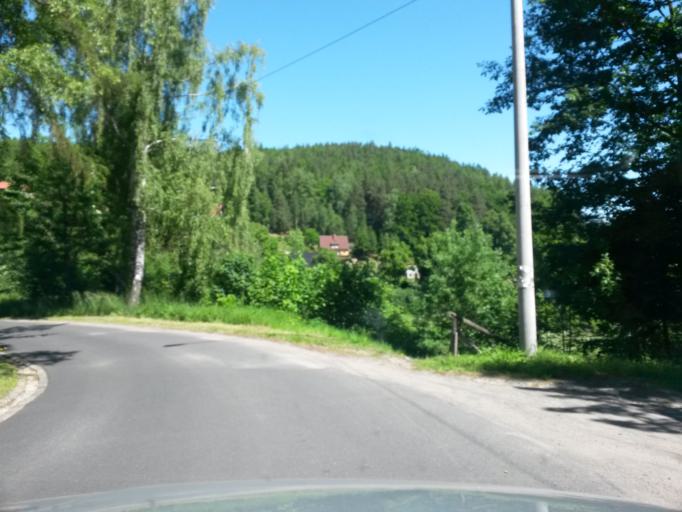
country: PL
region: Lower Silesian Voivodeship
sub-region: Powiat jeleniogorski
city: Podgorzyn
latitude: 50.8214
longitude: 15.6570
